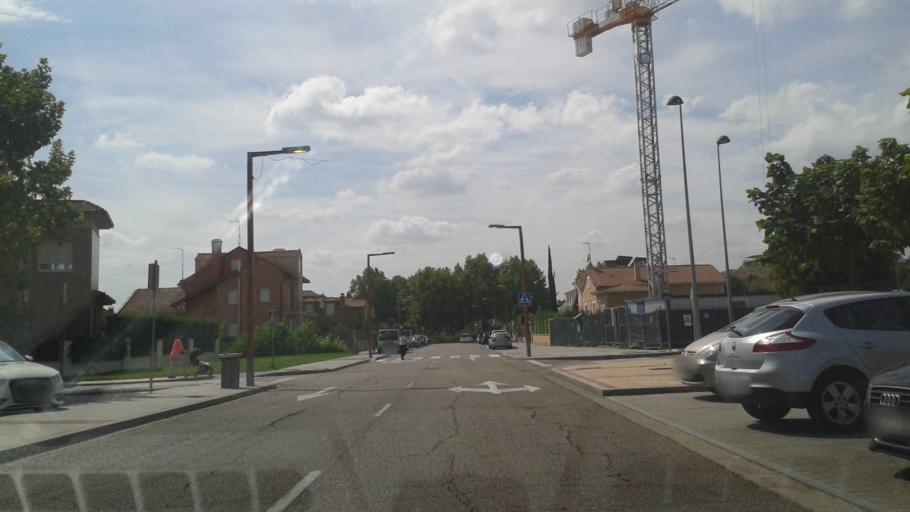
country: ES
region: Castille and Leon
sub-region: Provincia de Valladolid
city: Arroyo
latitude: 41.6186
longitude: -4.7814
